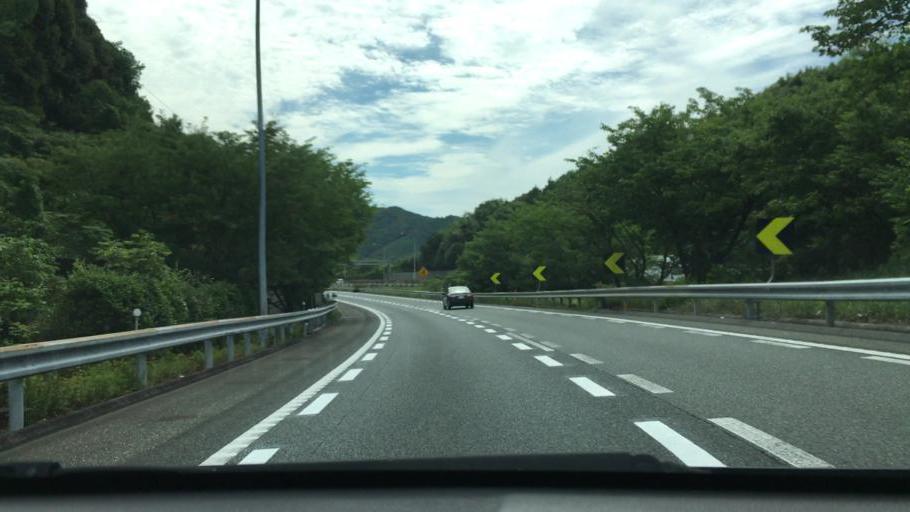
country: JP
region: Yamaguchi
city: Yamaguchi-shi
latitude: 34.1321
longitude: 131.4489
